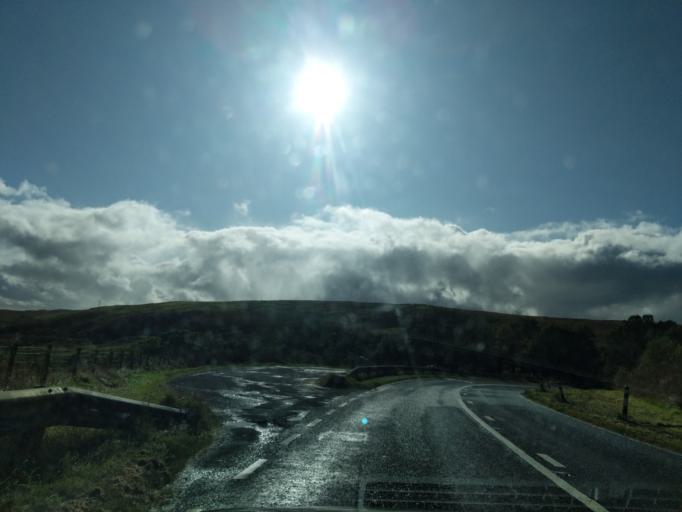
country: GB
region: Scotland
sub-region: Dumfries and Galloway
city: Moffat
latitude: 55.3644
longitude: -3.4761
